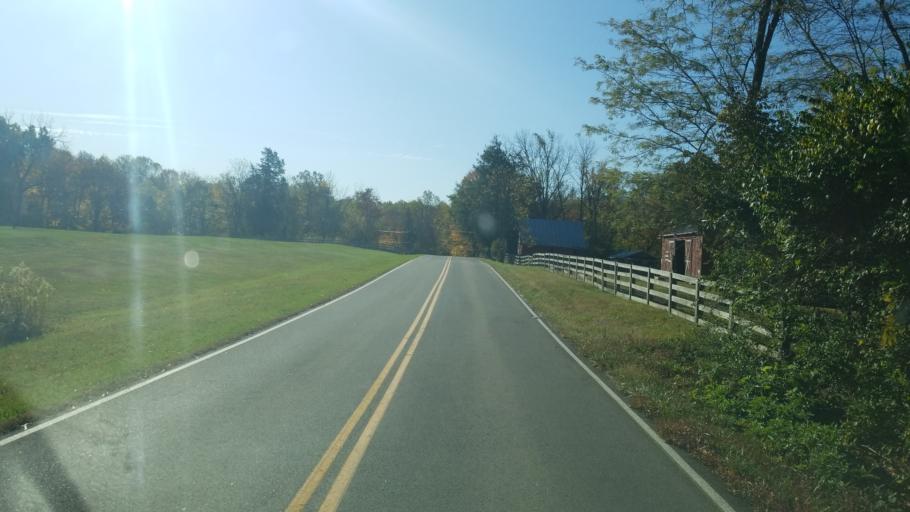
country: US
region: Ohio
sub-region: Warren County
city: Morrow
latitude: 39.4220
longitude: -84.0858
